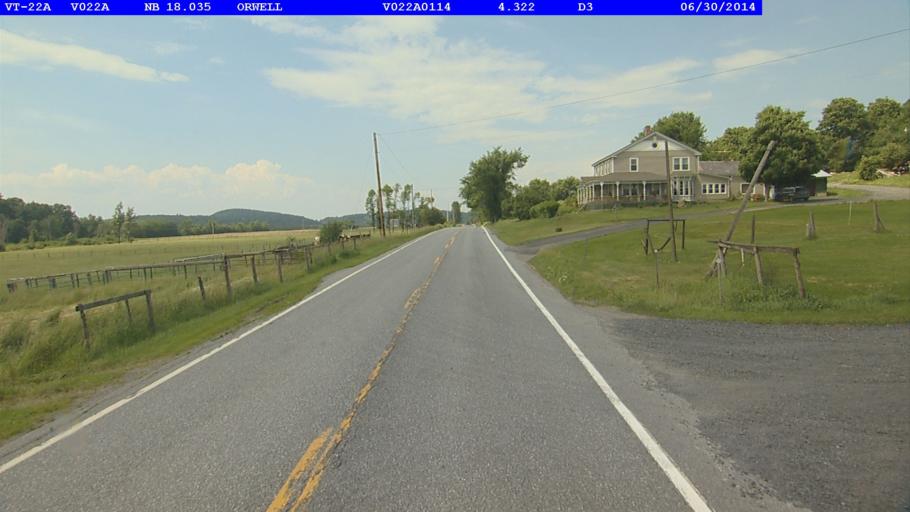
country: US
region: New York
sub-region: Essex County
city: Ticonderoga
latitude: 43.8191
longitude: -73.3063
